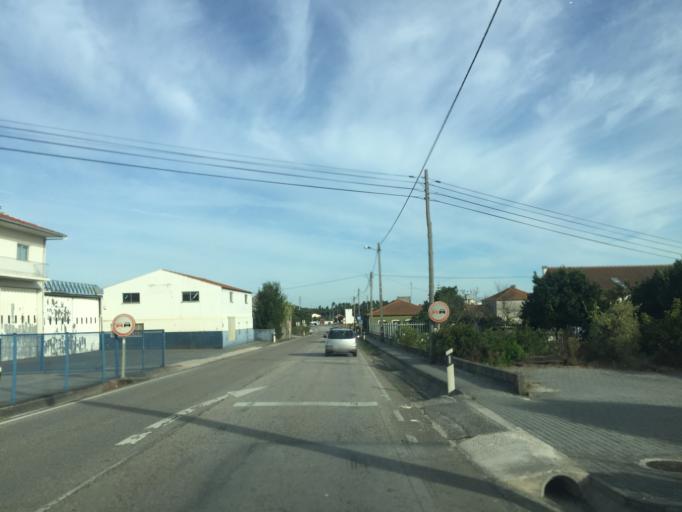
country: PT
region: Leiria
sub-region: Pombal
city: Lourical
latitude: 39.9662
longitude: -8.7915
